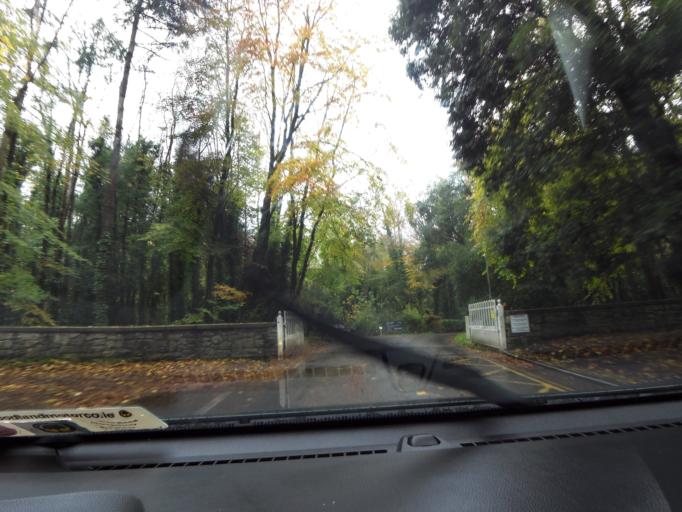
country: IE
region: Connaught
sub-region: County Galway
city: Gort
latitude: 53.0894
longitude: -8.8343
